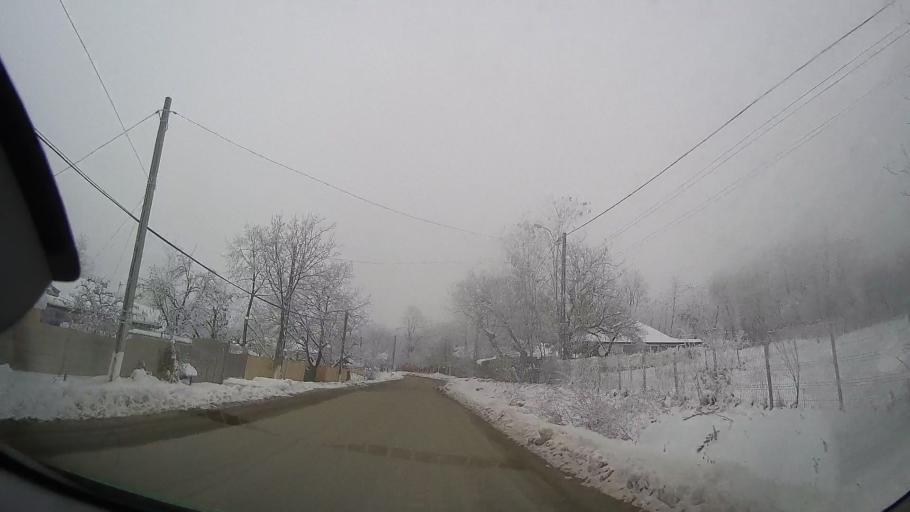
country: RO
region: Iasi
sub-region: Comuna Tansa
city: Tansa
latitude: 46.9052
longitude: 27.2425
